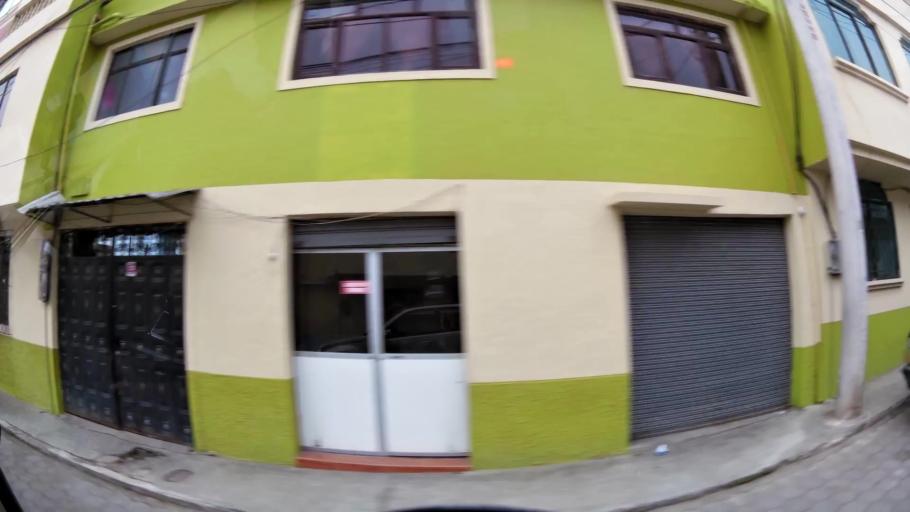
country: EC
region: Chimborazo
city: Alausi
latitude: -2.2898
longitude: -78.9182
